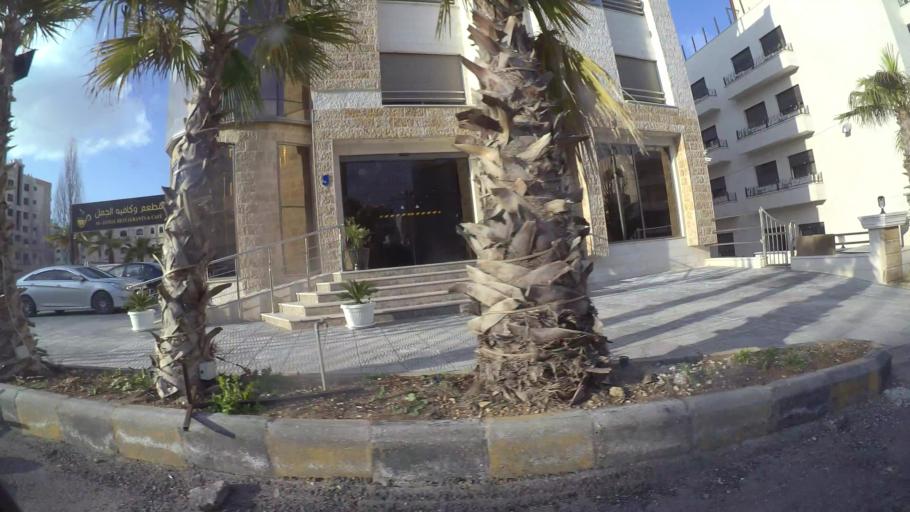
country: JO
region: Amman
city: Al Jubayhah
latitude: 32.0043
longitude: 35.8712
